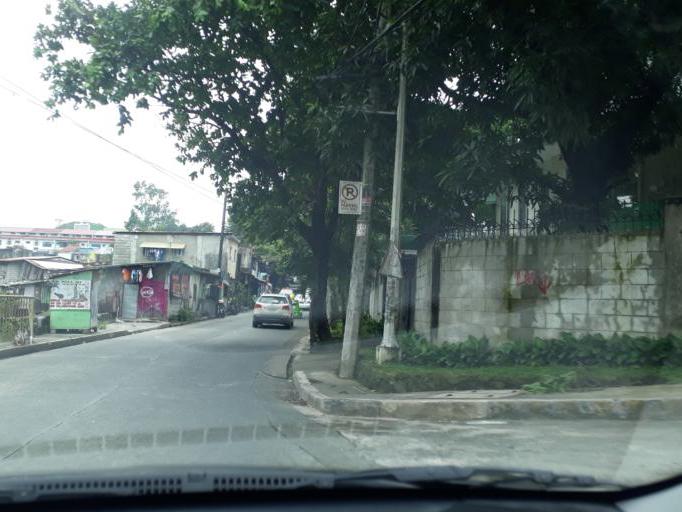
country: PH
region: Calabarzon
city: Del Monte
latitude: 14.6259
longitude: 121.0242
